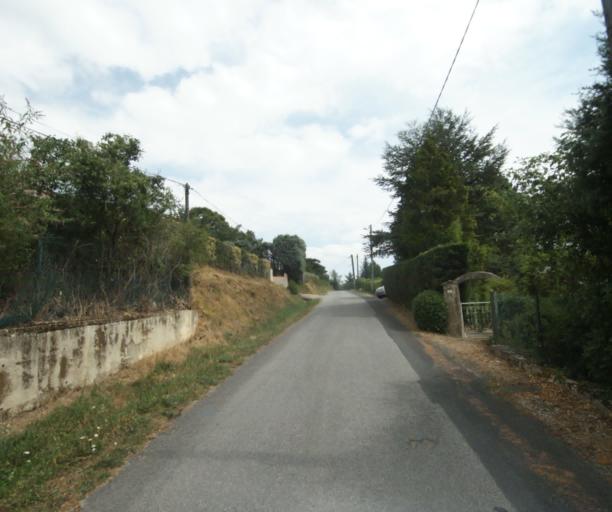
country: FR
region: Midi-Pyrenees
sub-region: Departement du Tarn
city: Soreze
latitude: 43.4368
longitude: 2.0411
